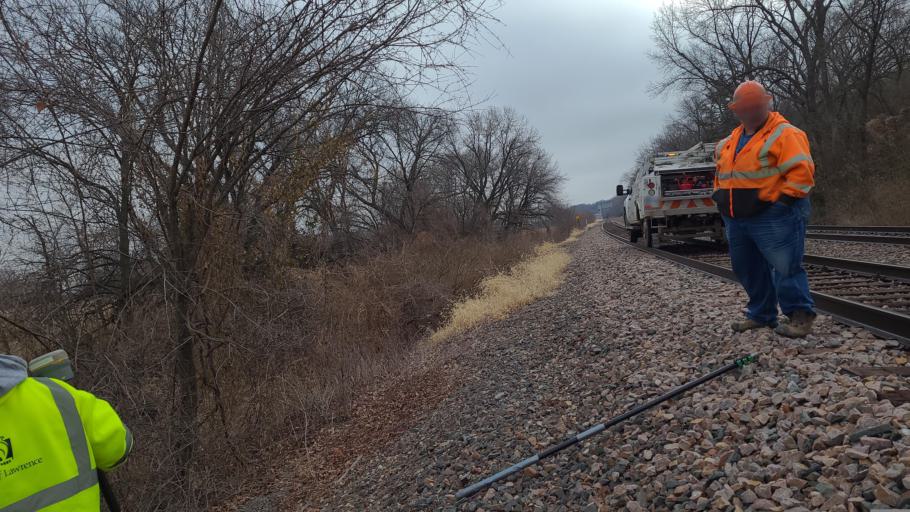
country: US
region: Kansas
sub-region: Douglas County
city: Lawrence
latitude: 38.9620
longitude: -95.2100
